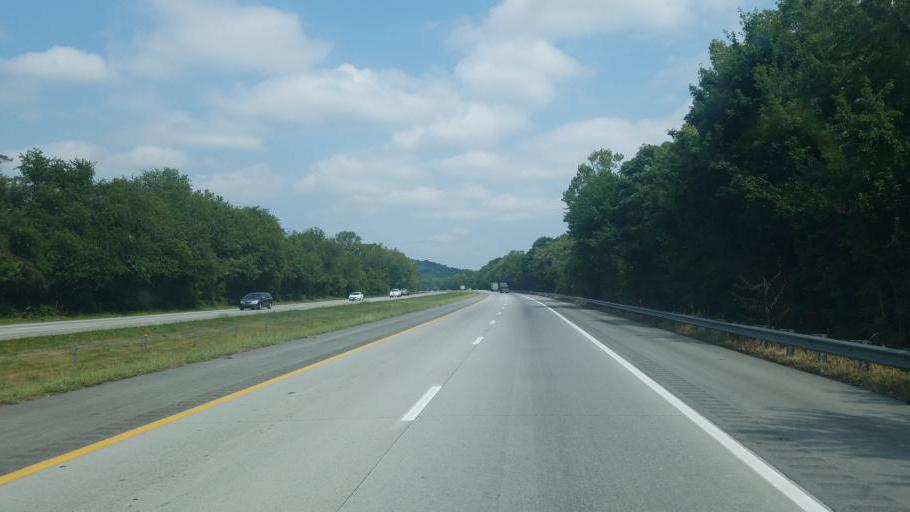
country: US
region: North Carolina
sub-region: Yadkin County
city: Jonesville
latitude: 36.1675
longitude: -80.8083
